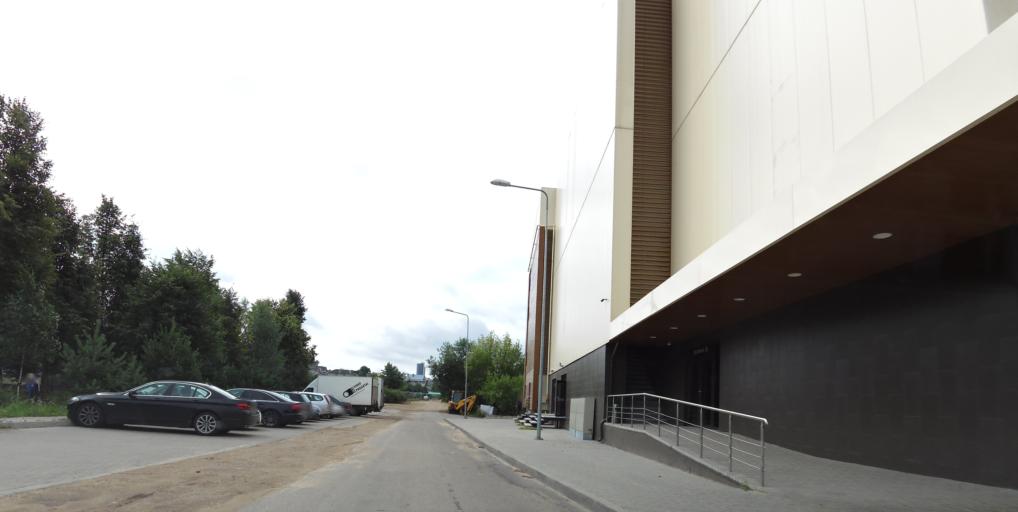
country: LT
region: Vilnius County
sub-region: Vilnius
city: Vilnius
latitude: 54.7119
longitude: 25.2771
